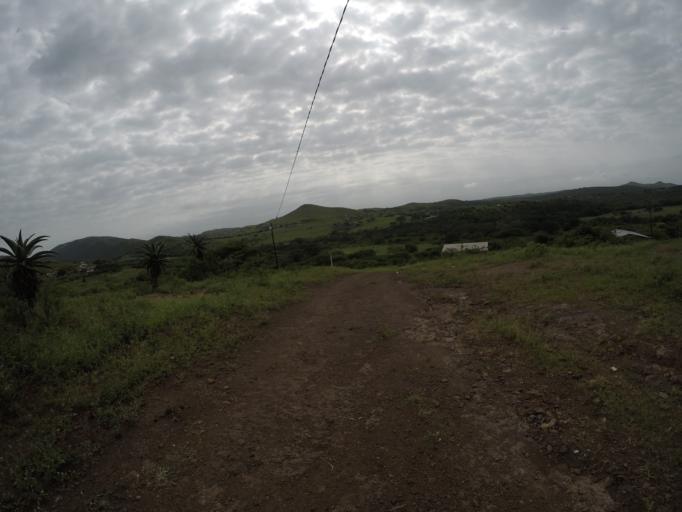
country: ZA
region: KwaZulu-Natal
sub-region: uThungulu District Municipality
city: Empangeni
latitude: -28.6271
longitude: 31.9091
